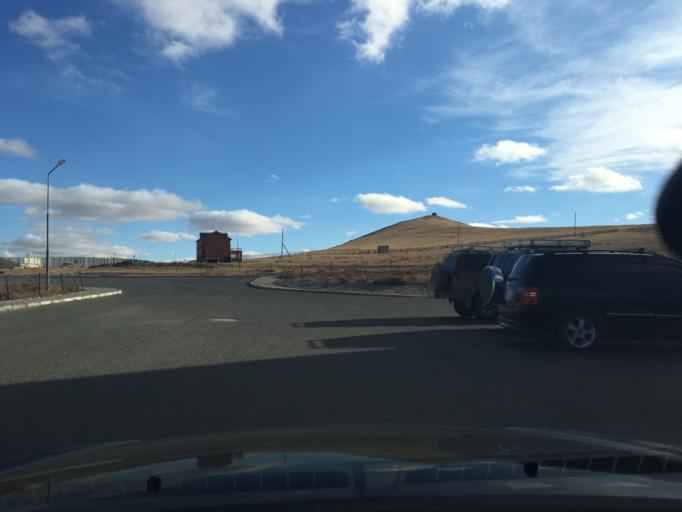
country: MN
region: Ulaanbaatar
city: Ulaanbaatar
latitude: 47.7897
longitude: 106.7455
